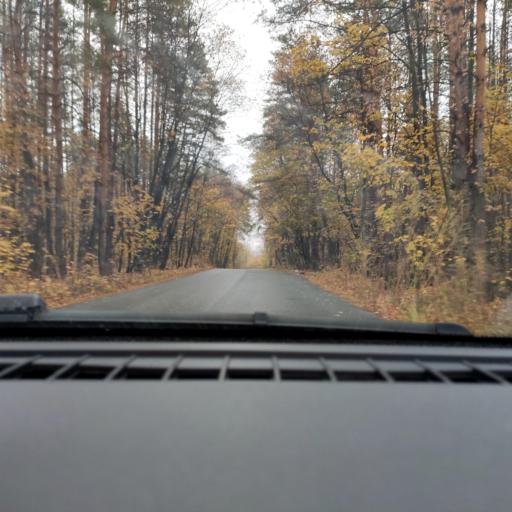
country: RU
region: Voronezj
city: Somovo
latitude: 51.6874
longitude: 39.2975
